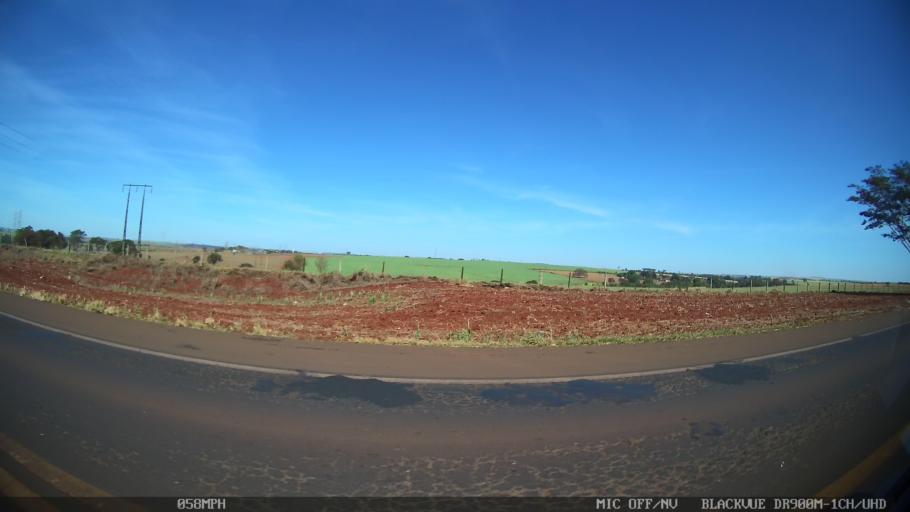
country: BR
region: Sao Paulo
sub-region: Sao Joaquim Da Barra
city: Sao Joaquim da Barra
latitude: -20.5226
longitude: -47.8531
